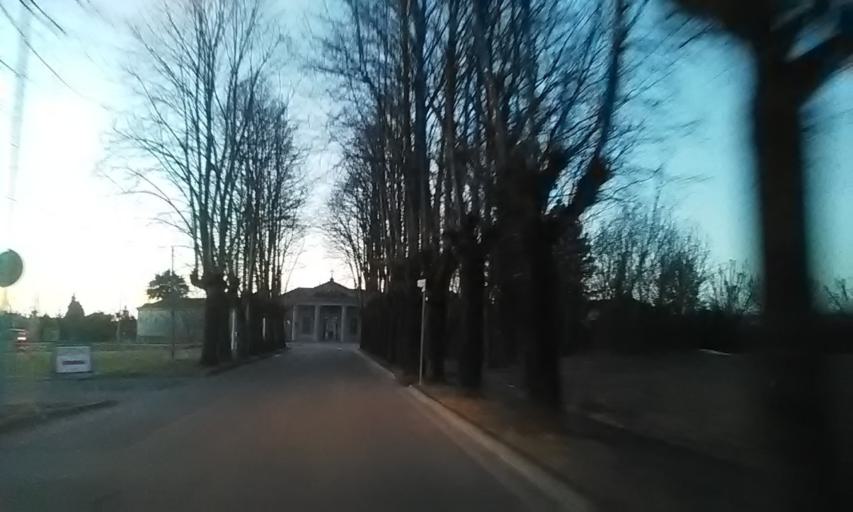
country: IT
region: Piedmont
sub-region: Provincia di Biella
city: Occhieppo Inferiore
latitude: 45.5518
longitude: 8.0371
